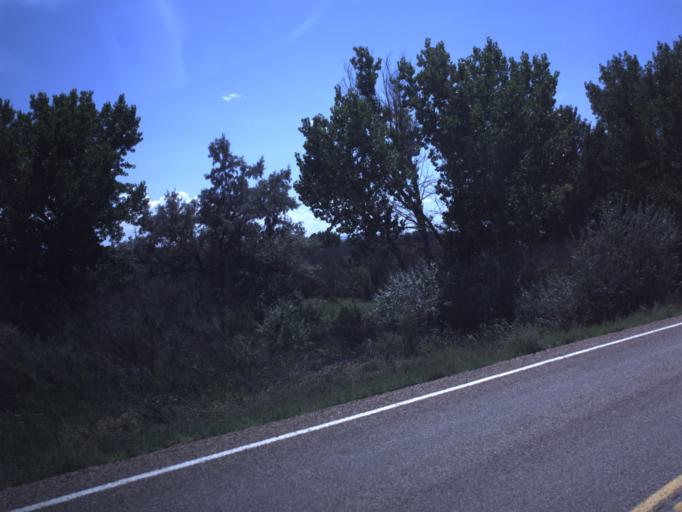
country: US
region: Utah
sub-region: Uintah County
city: Naples
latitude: 40.1020
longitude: -109.6737
